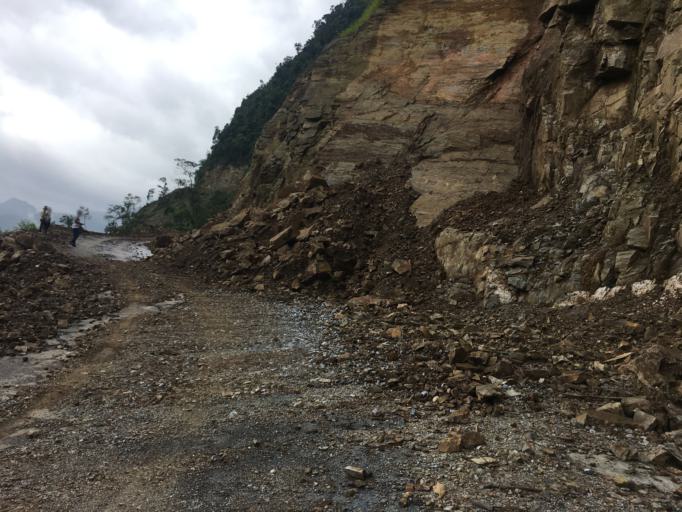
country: VN
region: Ha Giang
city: Thi Tran Tam Son
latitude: 22.9820
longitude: 105.0618
